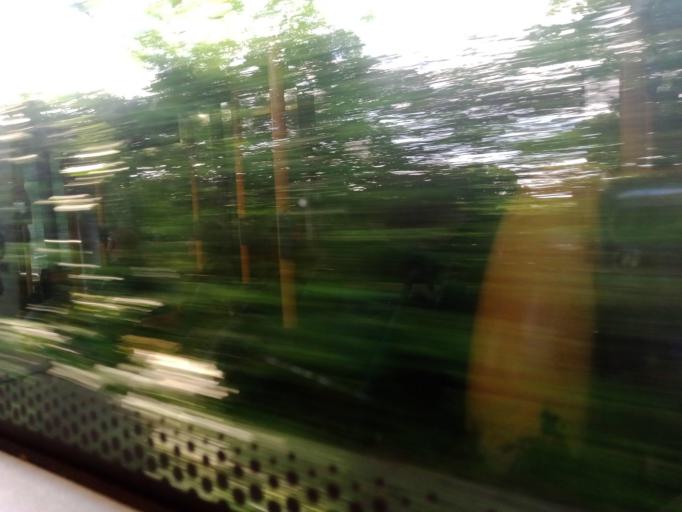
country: GB
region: Wales
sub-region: Anglesey
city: Llangoed
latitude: 53.2969
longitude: -4.0840
